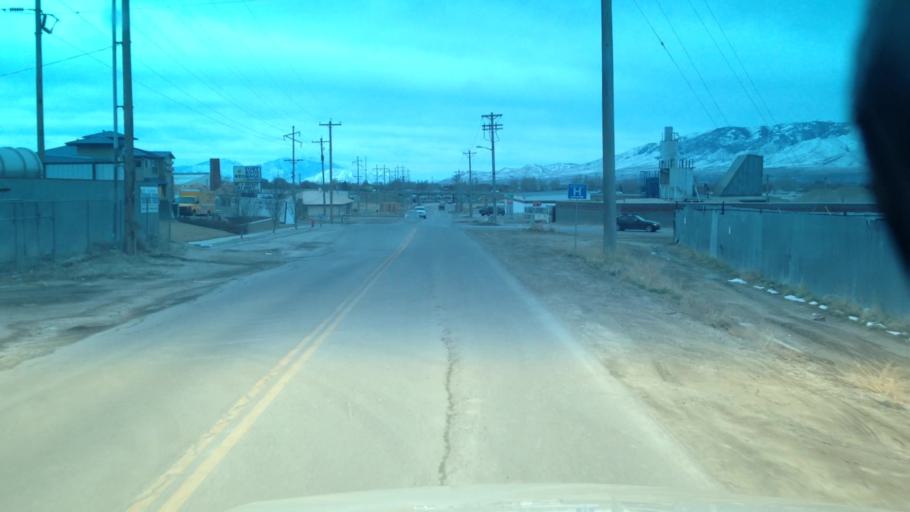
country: US
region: Utah
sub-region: Utah County
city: Lehi
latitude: 40.4191
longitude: -111.8688
